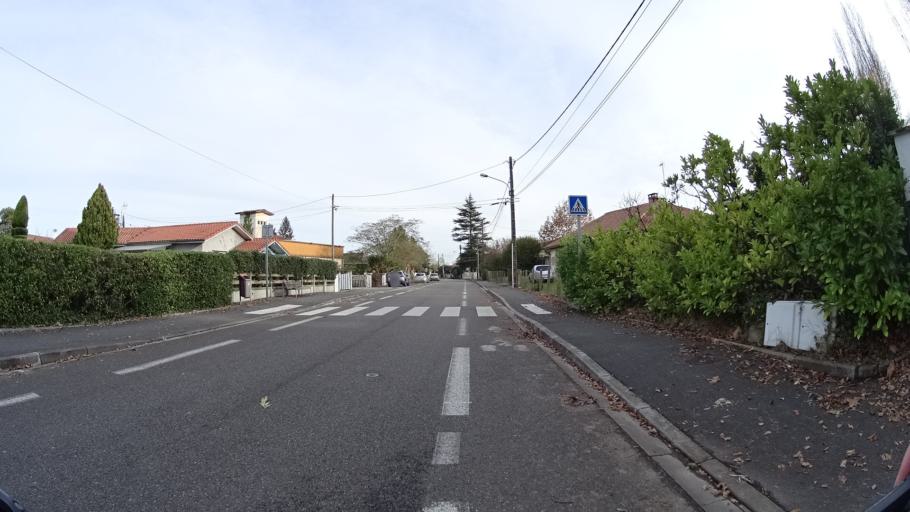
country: FR
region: Aquitaine
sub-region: Departement des Landes
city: Saint-Paul-les-Dax
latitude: 43.7307
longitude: -1.0474
